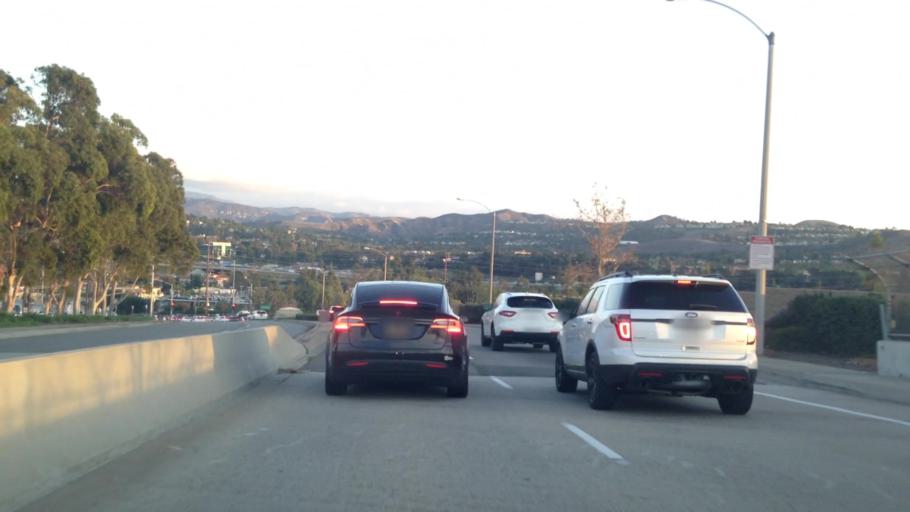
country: US
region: California
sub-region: Orange County
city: Yorba Linda
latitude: 33.8761
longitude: -117.7531
